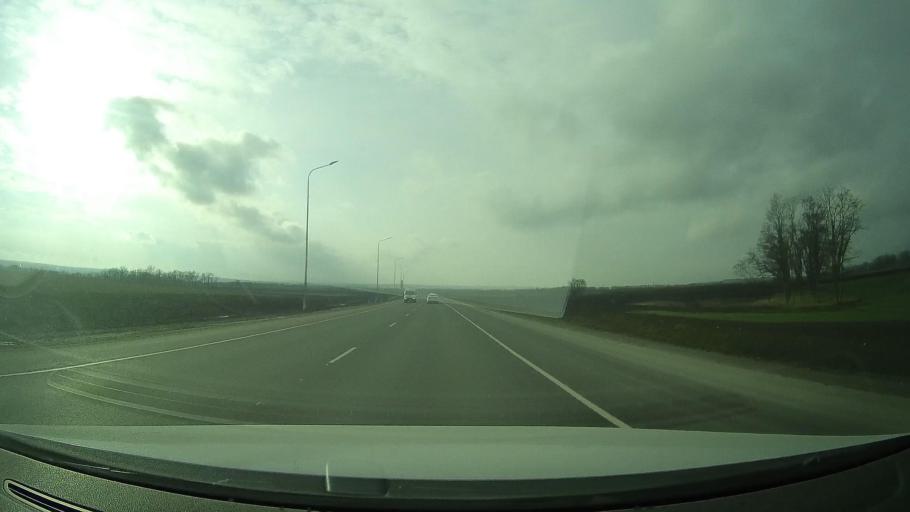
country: RU
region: Rostov
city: Grushevskaya
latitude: 47.4658
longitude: 39.8947
